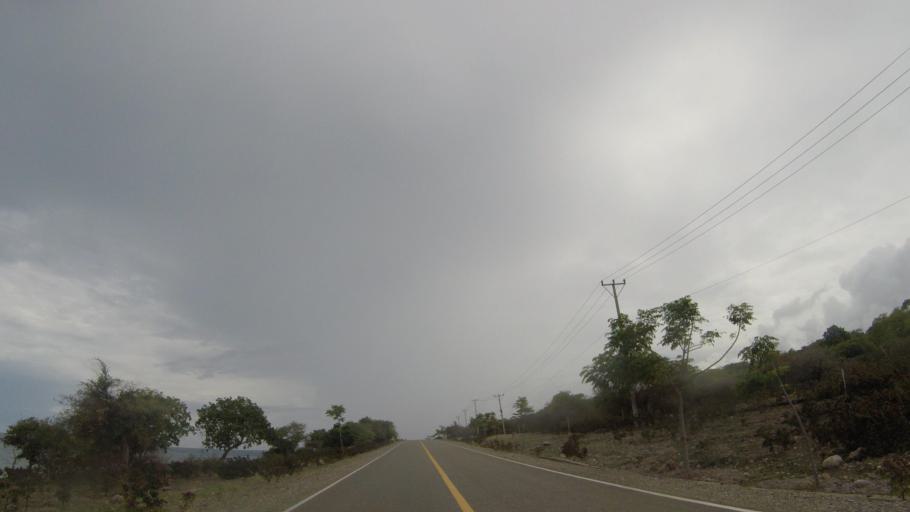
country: TL
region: Lautem
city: Lospalos
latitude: -8.4188
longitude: 126.7760
